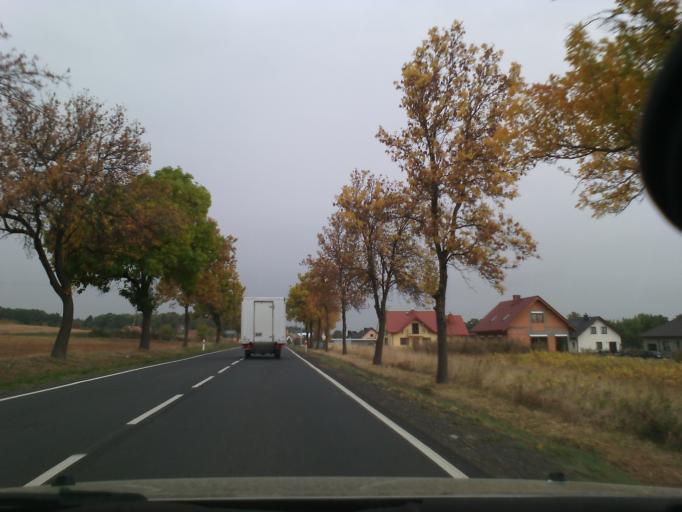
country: PL
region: Lower Silesian Voivodeship
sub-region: Powiat swidnicki
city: Swiebodzice
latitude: 50.8913
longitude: 16.2634
